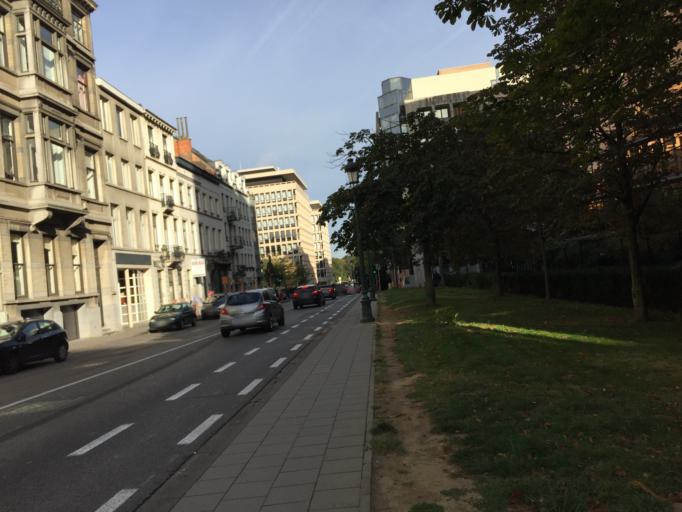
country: BE
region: Brussels Capital
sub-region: Bruxelles-Capitale
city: Brussels
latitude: 50.8386
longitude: 4.3682
